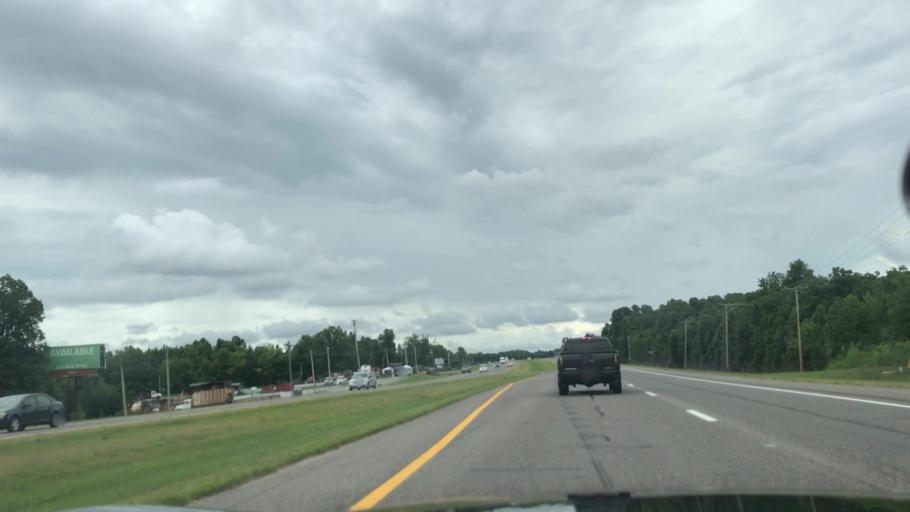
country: US
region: Tennessee
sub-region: Fentress County
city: Jamestown
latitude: 36.3644
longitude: -84.9464
